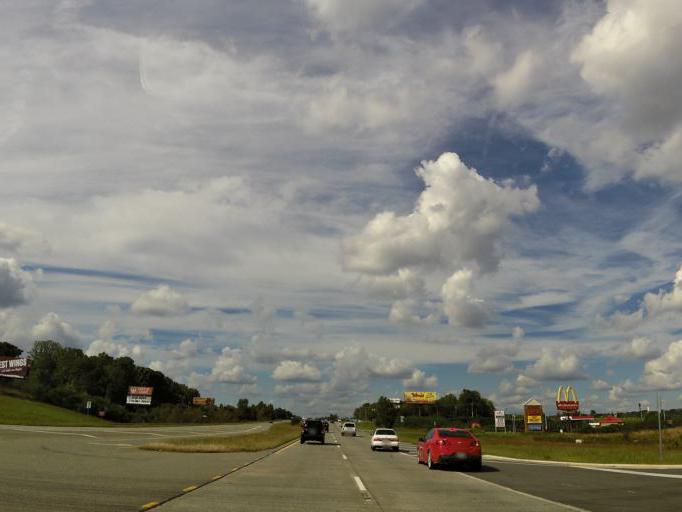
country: US
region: Georgia
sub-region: Pickens County
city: Jasper
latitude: 34.4619
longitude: -84.4566
